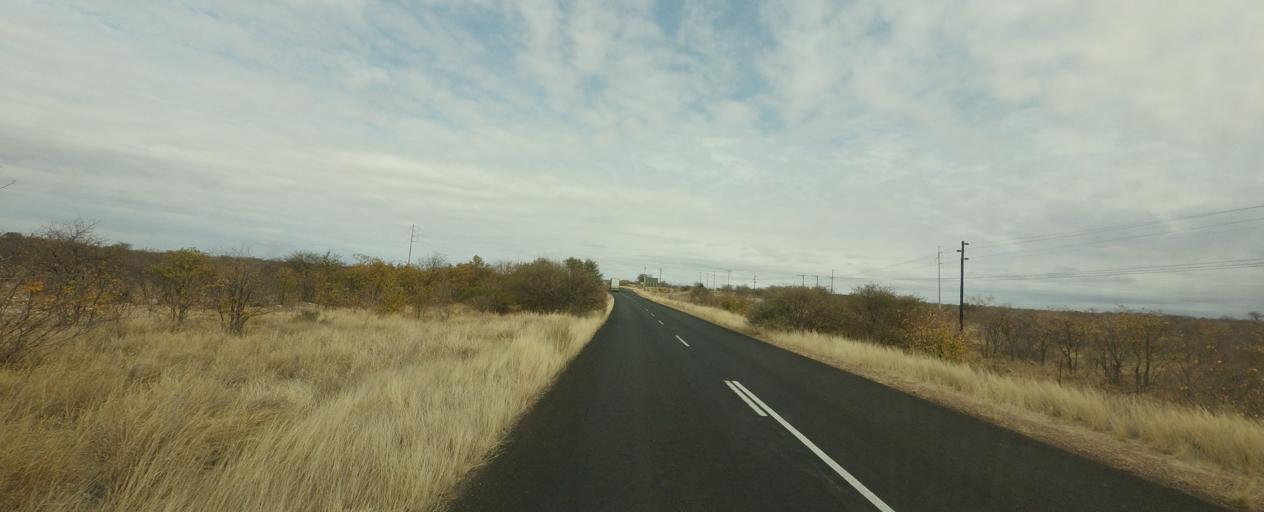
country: ZW
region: Matabeleland South
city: Beitbridge
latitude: -22.4295
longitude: 29.4221
